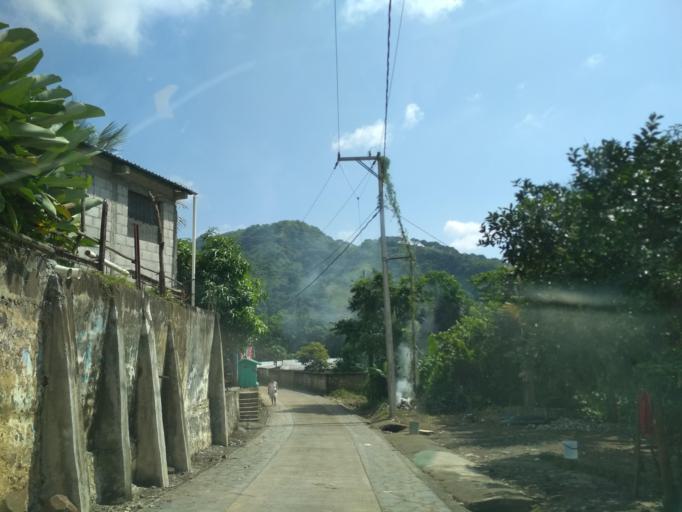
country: MX
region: Veracruz
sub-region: San Andres Tuxtla
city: Texcaltitan Xoteapan (Texcaltitan)
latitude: 18.4484
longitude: -95.2566
